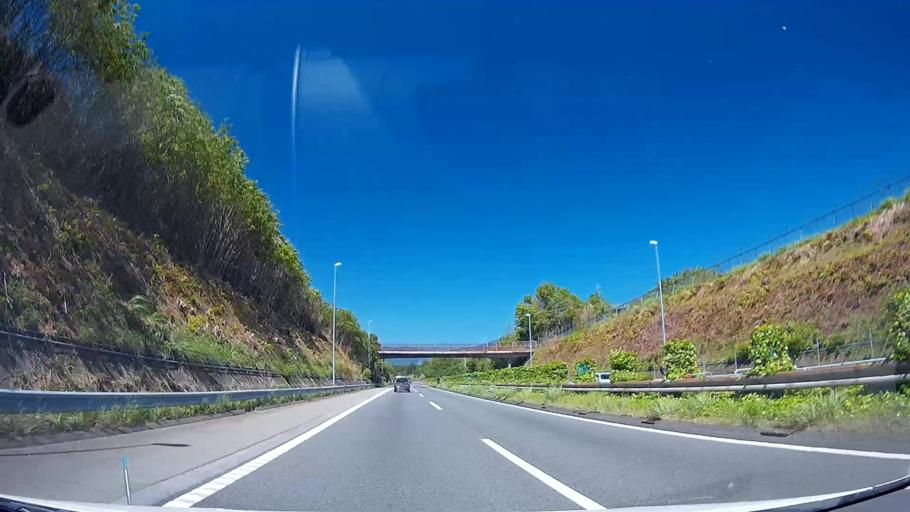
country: JP
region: Shizuoka
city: Mishima
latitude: 35.1674
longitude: 138.8923
